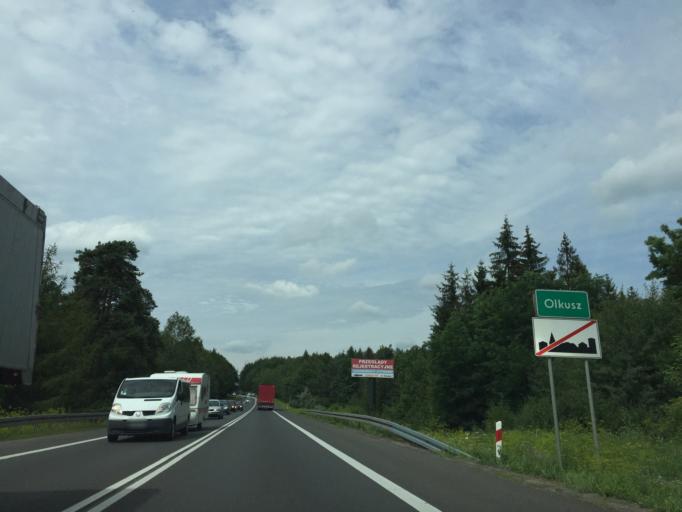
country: PL
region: Lesser Poland Voivodeship
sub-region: Powiat olkuski
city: Osiek
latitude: 50.2688
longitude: 19.6043
